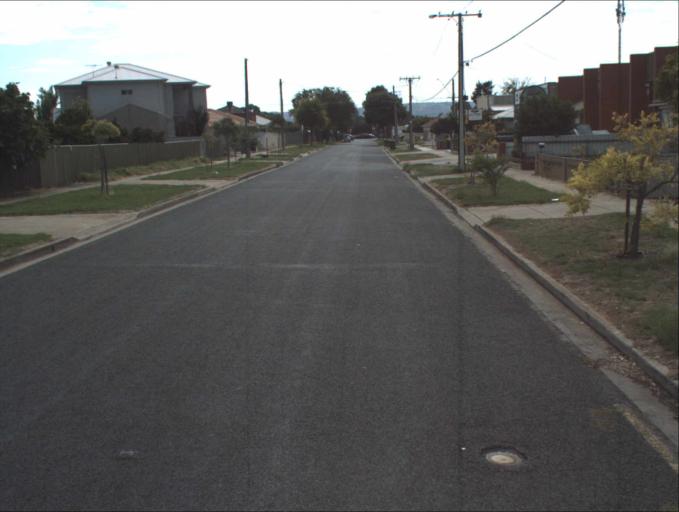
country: AU
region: South Australia
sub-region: Port Adelaide Enfield
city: Klemzig
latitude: -34.8806
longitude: 138.6328
